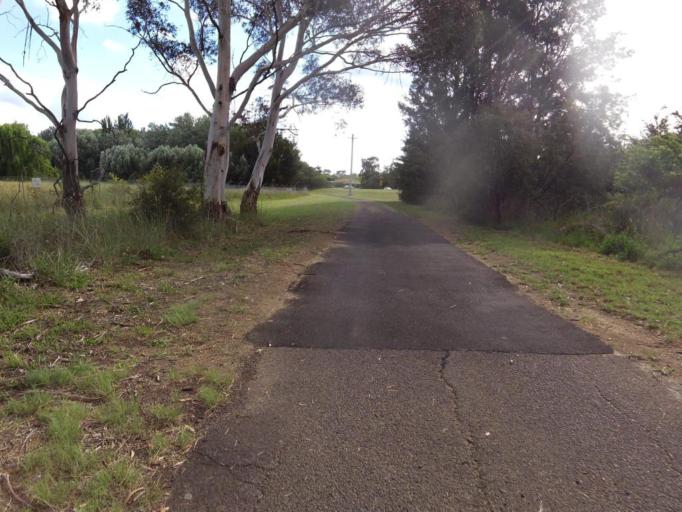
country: AU
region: Australian Capital Territory
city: Belconnen
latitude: -35.2186
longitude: 149.0816
